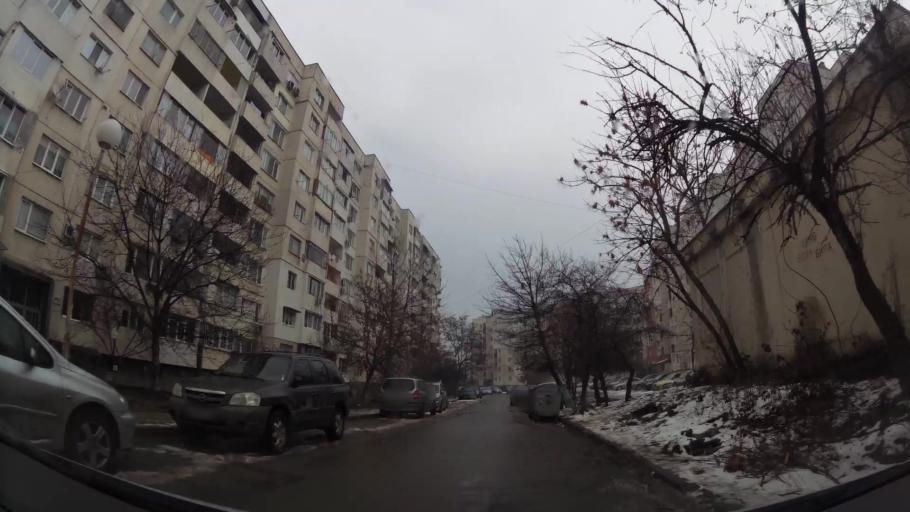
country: BG
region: Sofia-Capital
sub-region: Stolichna Obshtina
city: Sofia
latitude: 42.6866
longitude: 23.2579
